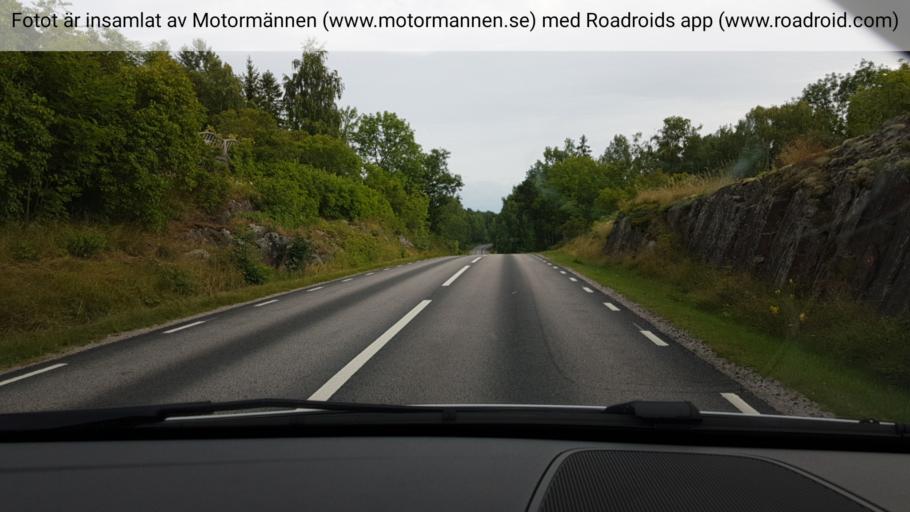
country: SE
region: Stockholm
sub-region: Norrtalje Kommun
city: Arno
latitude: 60.0278
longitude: 18.7873
